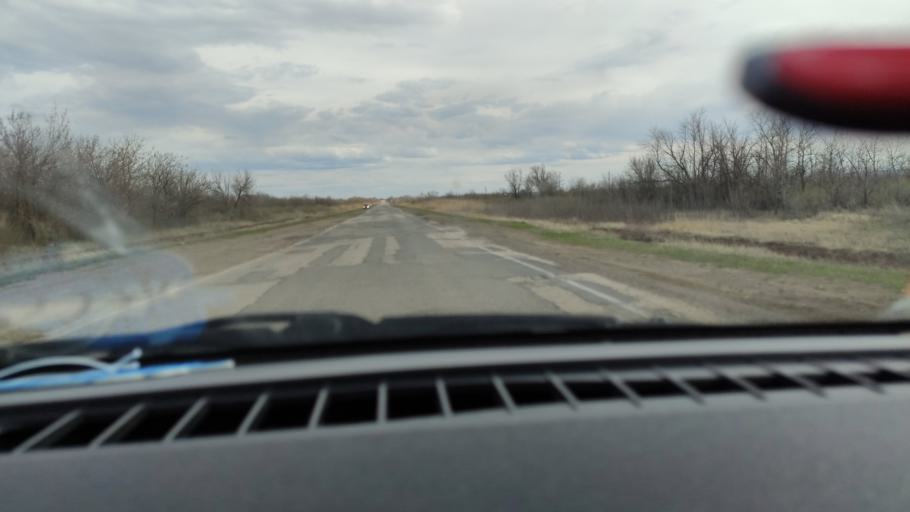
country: RU
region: Saratov
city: Rovnoye
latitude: 51.0082
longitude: 46.0999
